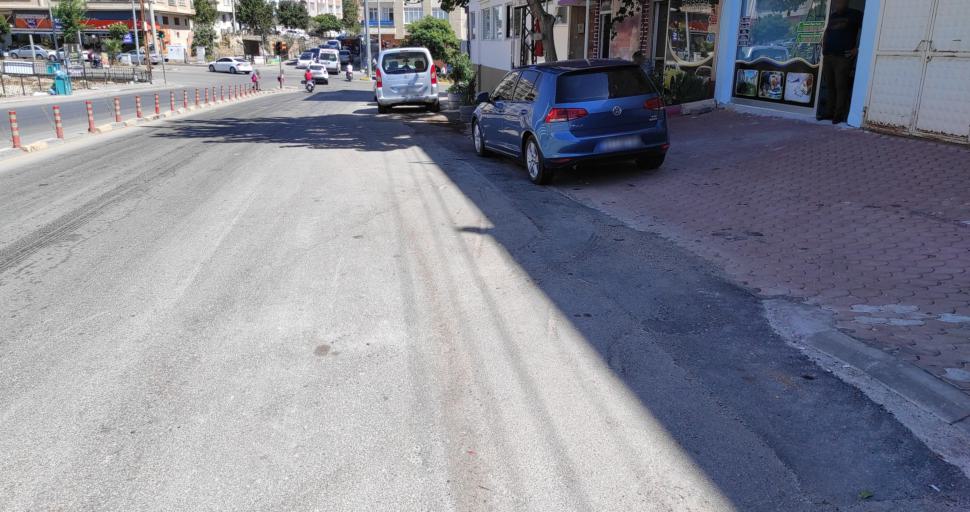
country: TR
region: Kilis
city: Kilis
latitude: 36.7239
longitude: 37.1037
